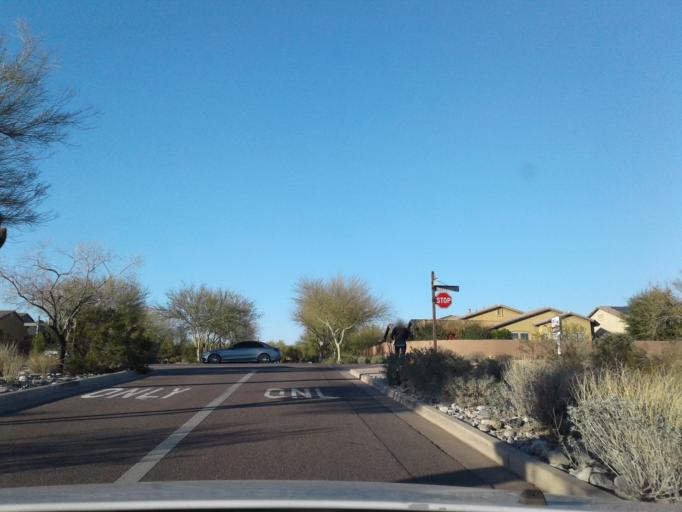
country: US
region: Arizona
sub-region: Maricopa County
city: Paradise Valley
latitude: 33.6458
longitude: -111.8832
